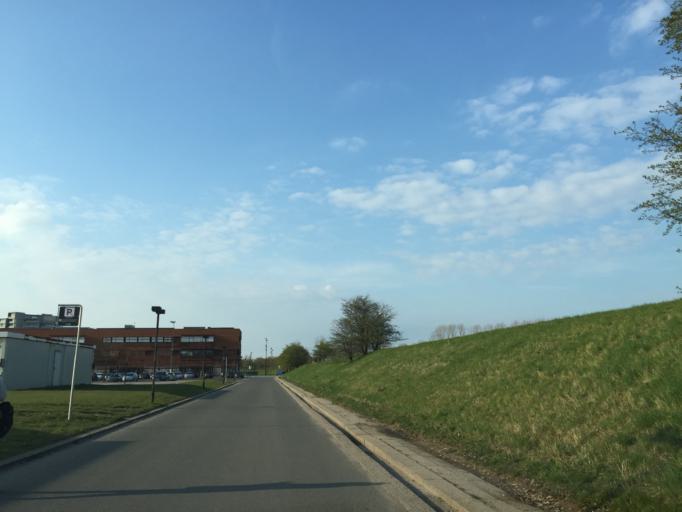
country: DK
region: South Denmark
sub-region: Odense Kommune
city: Neder Holluf
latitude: 55.3688
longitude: 10.4326
